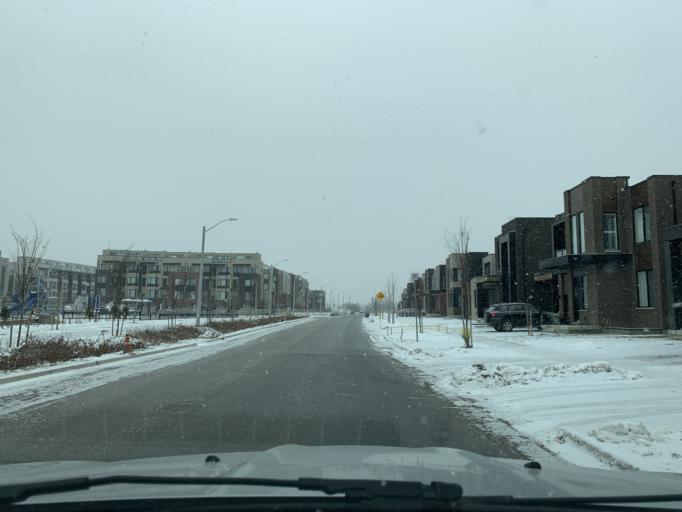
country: CA
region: Ontario
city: Concord
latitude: 43.7345
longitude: -79.4784
